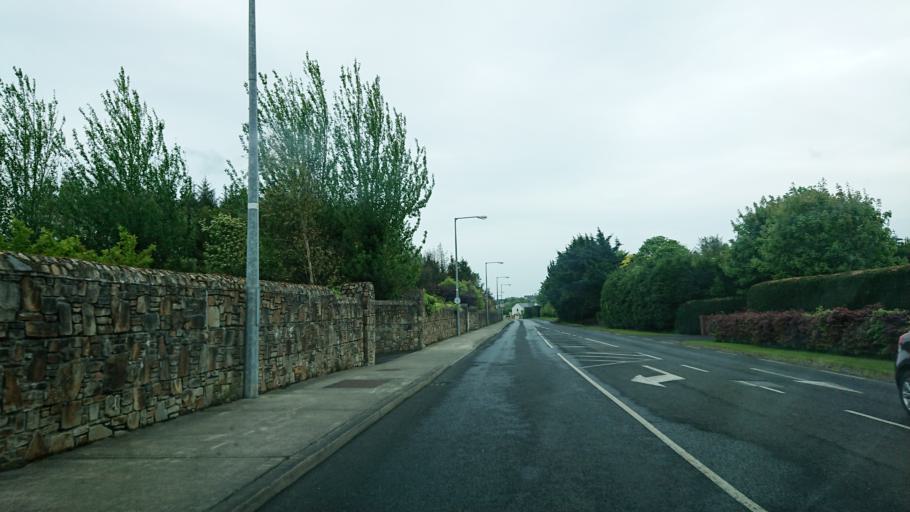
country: IE
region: Munster
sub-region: Waterford
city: Waterford
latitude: 52.2335
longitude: -7.0726
